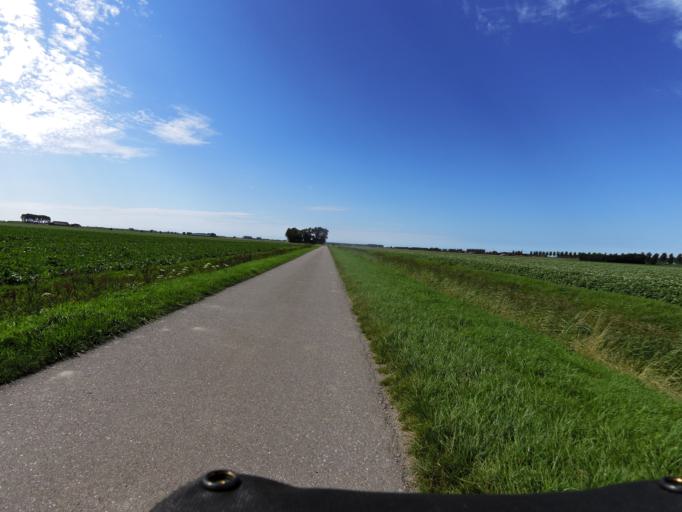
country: NL
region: Zeeland
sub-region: Gemeente Noord-Beveland
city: Kamperland
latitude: 51.5511
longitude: 3.7403
